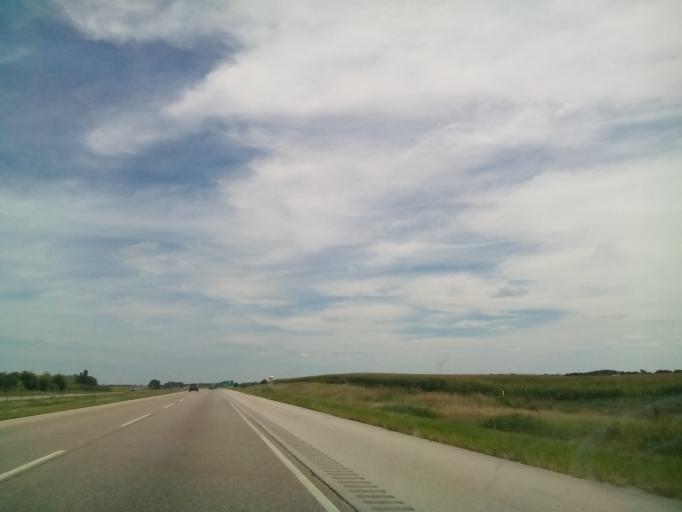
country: US
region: Illinois
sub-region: DeKalb County
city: Malta
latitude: 41.9001
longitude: -88.8061
